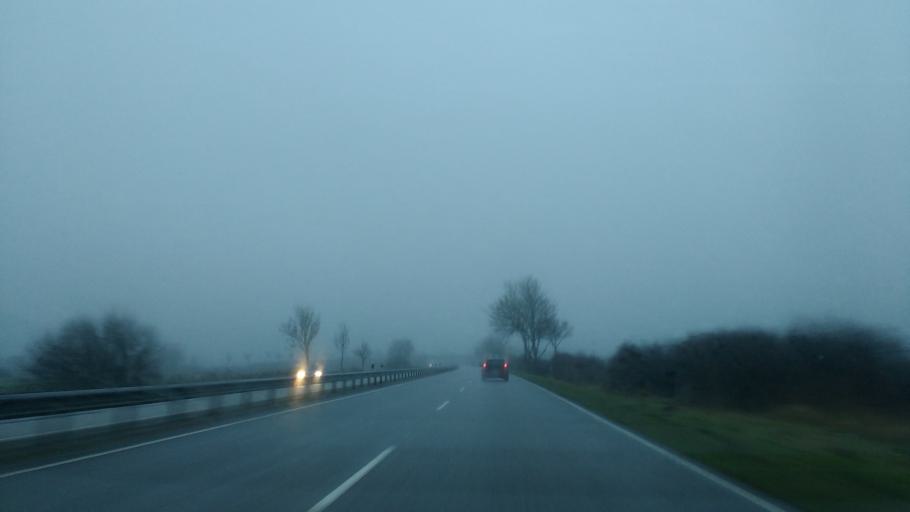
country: DE
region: Schleswig-Holstein
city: Jevenstedt
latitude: 54.2567
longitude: 9.6663
